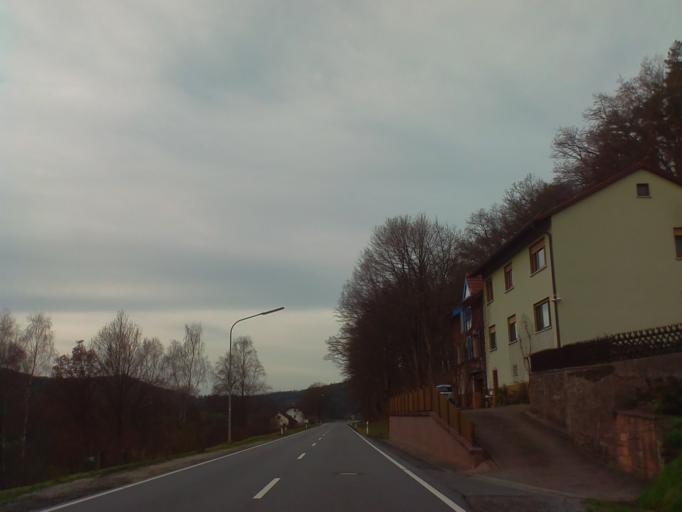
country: DE
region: Hesse
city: Reichelsheim
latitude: 49.6407
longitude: 8.8982
